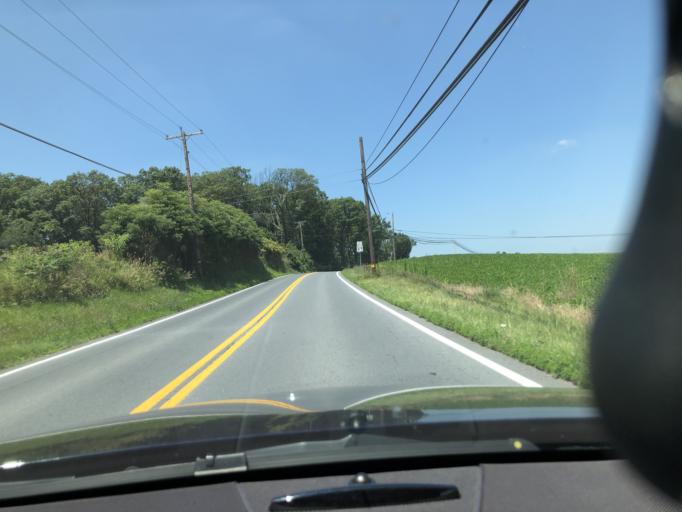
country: US
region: Maryland
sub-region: Carroll County
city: Westminster
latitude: 39.5201
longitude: -76.9869
